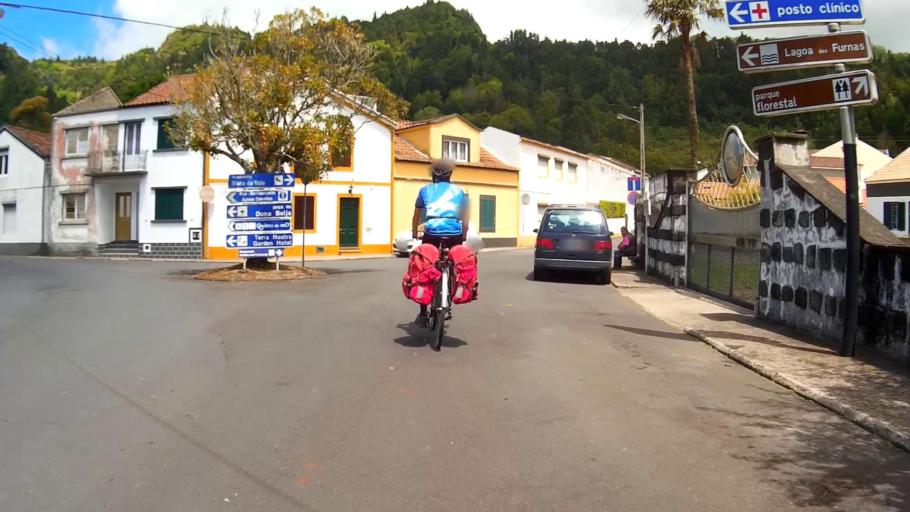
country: PT
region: Azores
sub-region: Povoacao
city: Furnas
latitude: 37.7760
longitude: -25.3124
